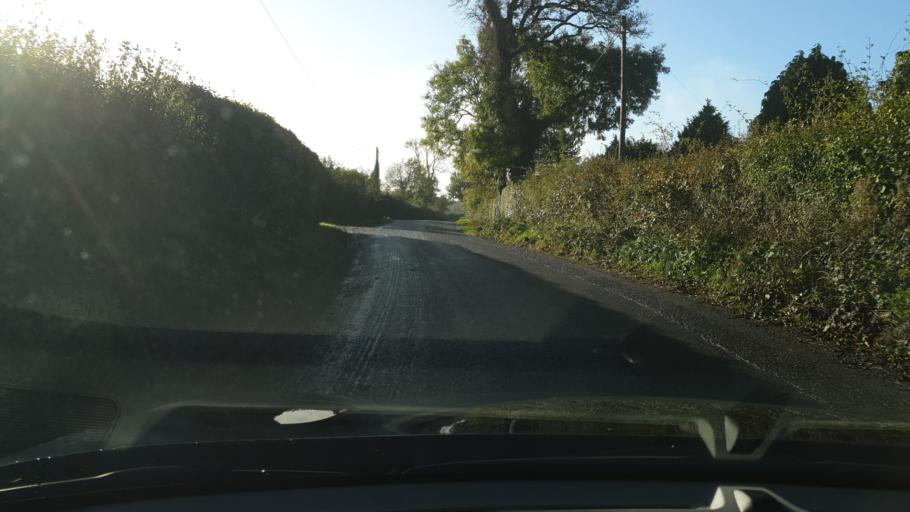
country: IE
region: Leinster
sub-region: An Mhi
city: Ashbourne
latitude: 53.4762
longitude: -6.3750
